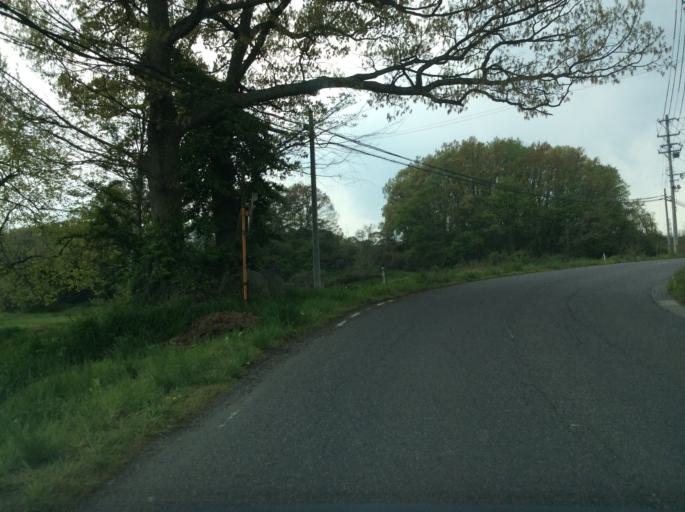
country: JP
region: Fukushima
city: Koriyama
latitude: 37.3831
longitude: 140.4211
